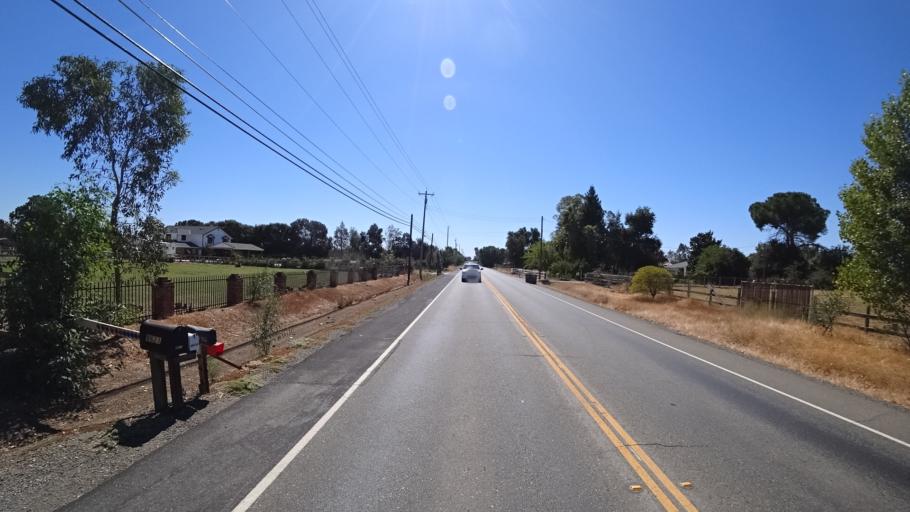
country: US
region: California
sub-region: Sacramento County
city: Vineyard
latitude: 38.4445
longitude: -121.3347
